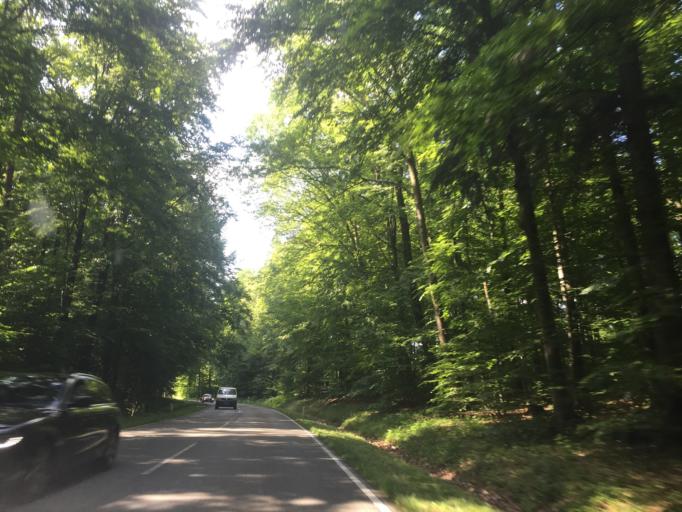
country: DE
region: Baden-Wuerttemberg
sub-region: Karlsruhe Region
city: Gaiberg
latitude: 49.3528
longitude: 8.7494
